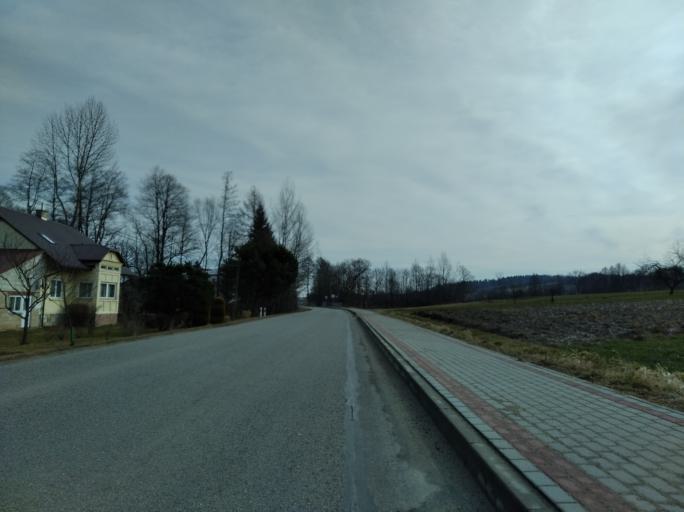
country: PL
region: Subcarpathian Voivodeship
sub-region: Powiat brzozowski
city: Orzechowka
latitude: 49.7274
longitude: 21.9481
